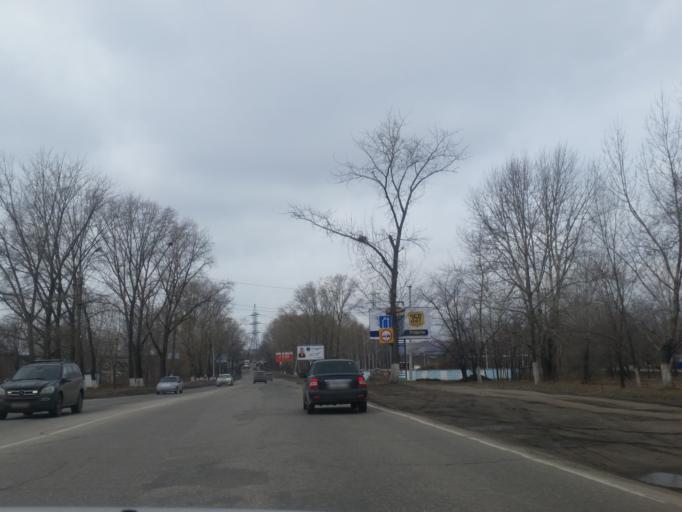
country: RU
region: Ulyanovsk
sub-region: Ulyanovskiy Rayon
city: Ulyanovsk
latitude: 54.3201
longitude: 48.4744
